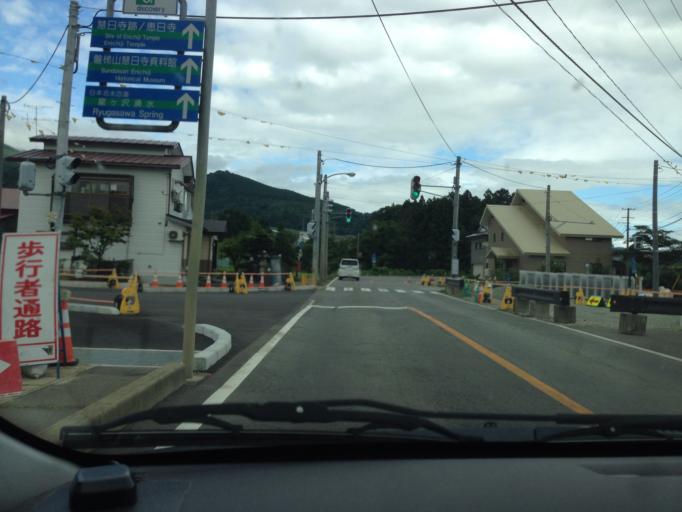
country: JP
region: Fukushima
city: Kitakata
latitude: 37.5772
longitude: 139.9472
